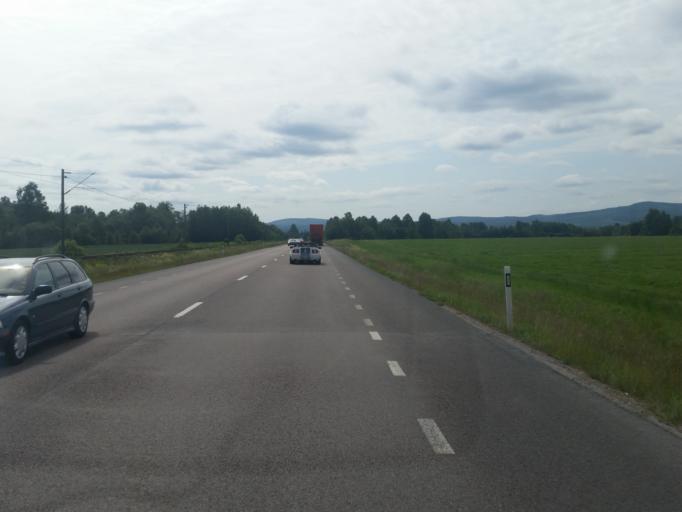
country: SE
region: Dalarna
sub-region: Gagnefs Kommun
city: Djuras
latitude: 60.5738
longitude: 15.1237
